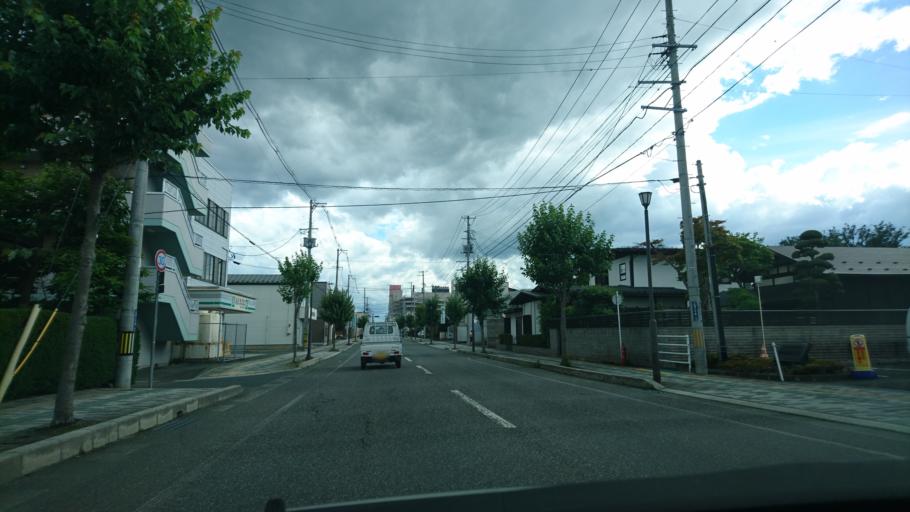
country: JP
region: Iwate
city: Kitakami
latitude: 39.2926
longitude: 141.1196
